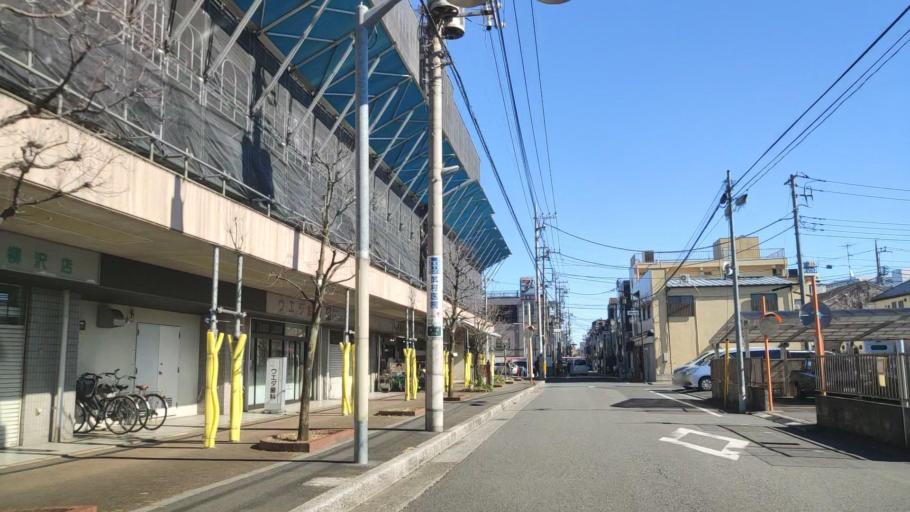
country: JP
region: Tokyo
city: Musashino
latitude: 35.7225
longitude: 139.5559
